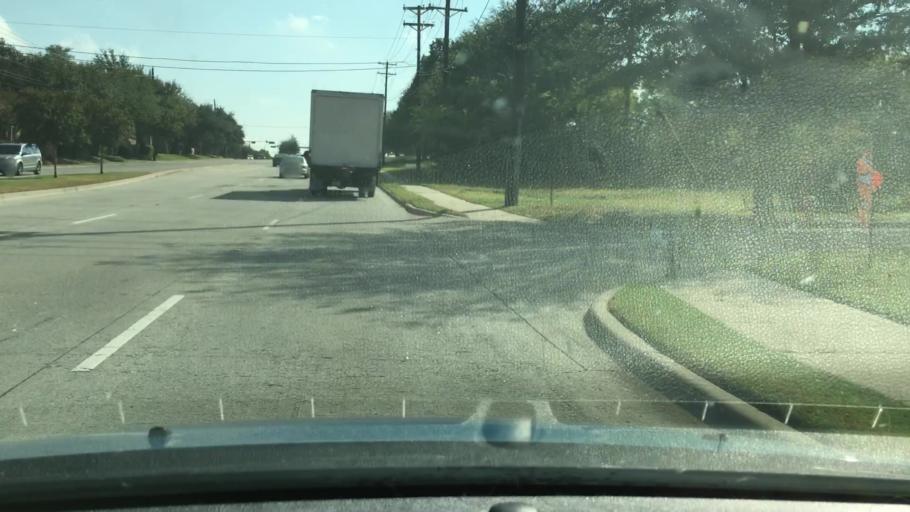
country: US
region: Texas
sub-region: Dallas County
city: Addison
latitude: 32.9870
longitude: -96.8506
